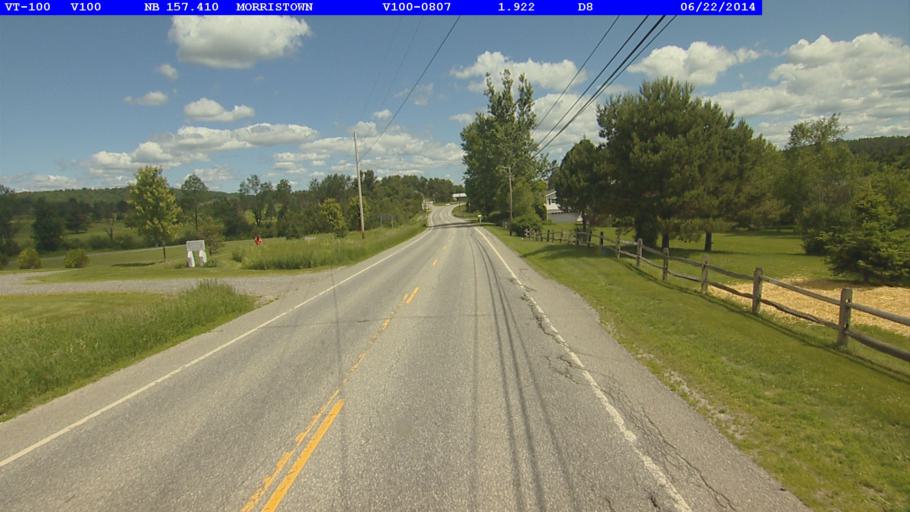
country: US
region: Vermont
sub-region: Lamoille County
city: Morristown
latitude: 44.5201
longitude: -72.6200
